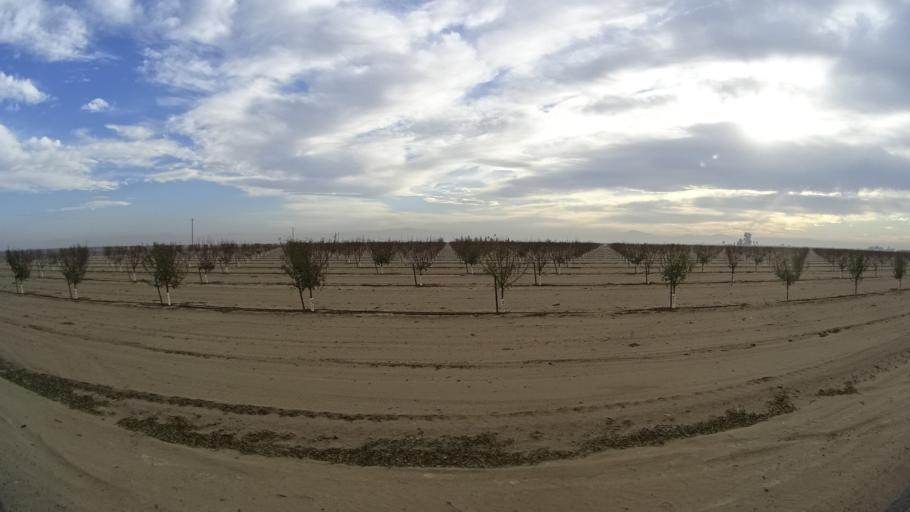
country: US
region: California
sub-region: Kern County
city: Rosedale
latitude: 35.4118
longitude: -119.1899
